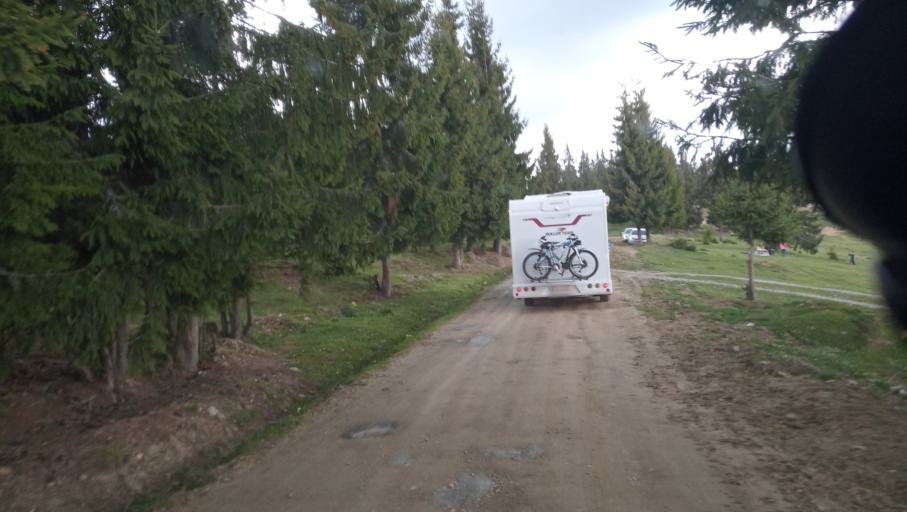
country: RO
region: Cluj
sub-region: Comuna Belis
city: Belis
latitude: 46.6339
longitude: 23.0434
